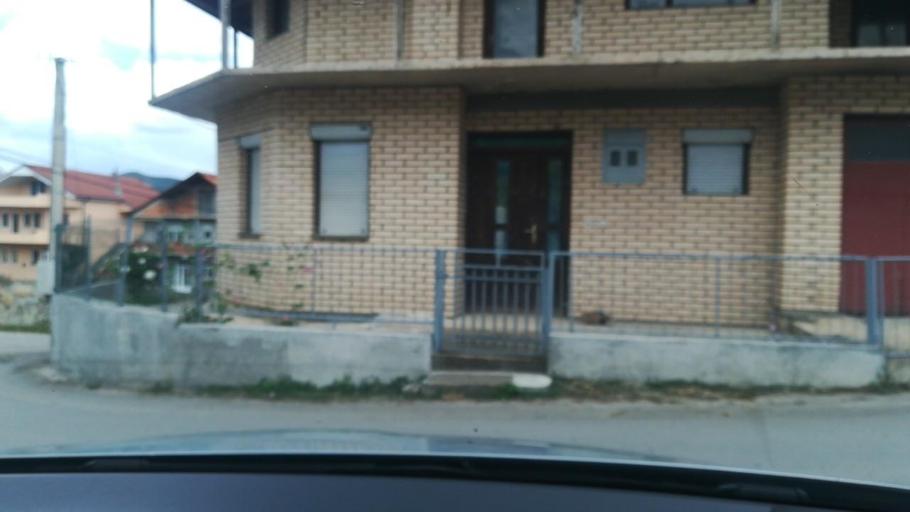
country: MK
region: Delcevo
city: Delcevo
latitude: 41.9687
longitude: 22.7652
